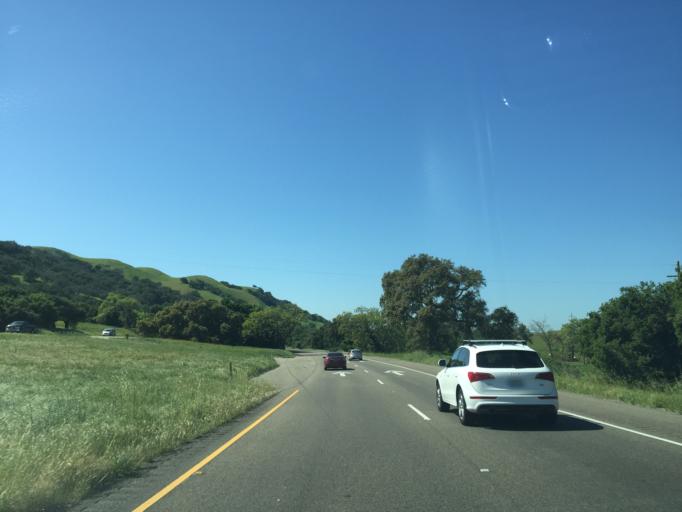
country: US
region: California
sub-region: Santa Barbara County
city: Los Olivos
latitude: 34.7104
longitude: -120.1781
